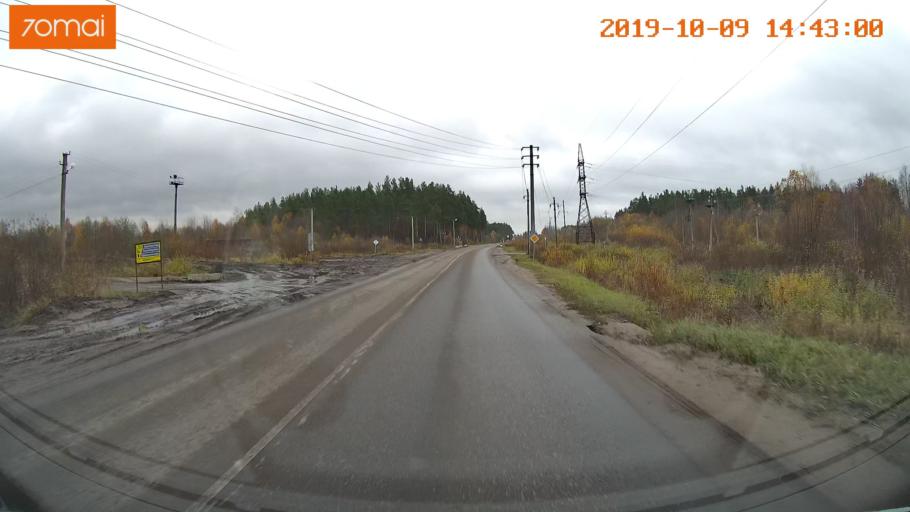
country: RU
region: Kostroma
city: Buy
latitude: 58.4588
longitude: 41.5398
